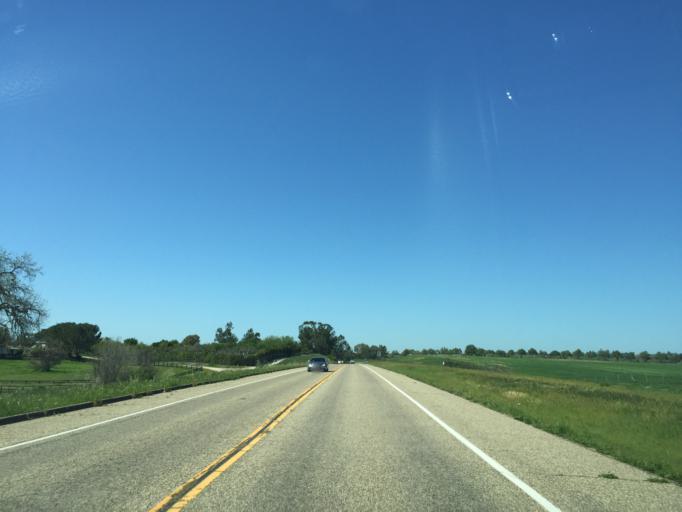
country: US
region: California
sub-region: Santa Barbara County
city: Santa Ynez
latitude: 34.6257
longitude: -120.0731
